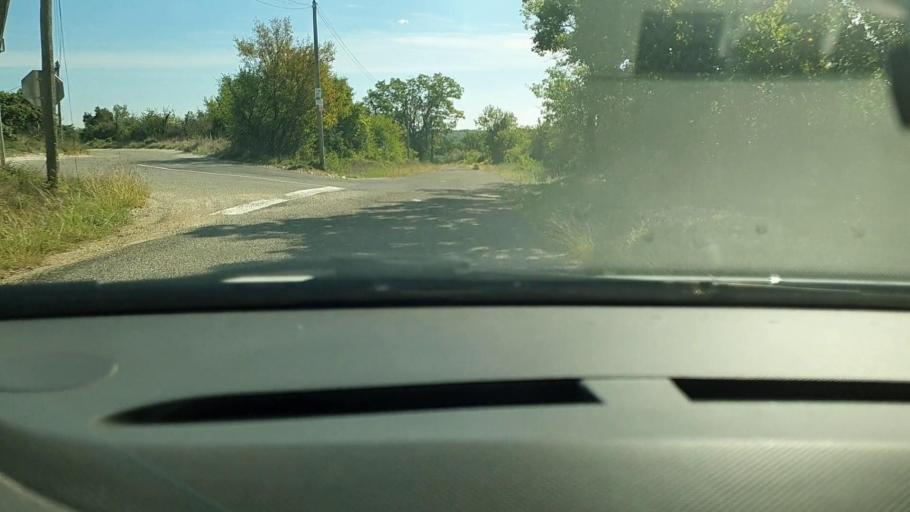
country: FR
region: Languedoc-Roussillon
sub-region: Departement du Gard
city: Barjac
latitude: 44.1908
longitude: 4.3221
